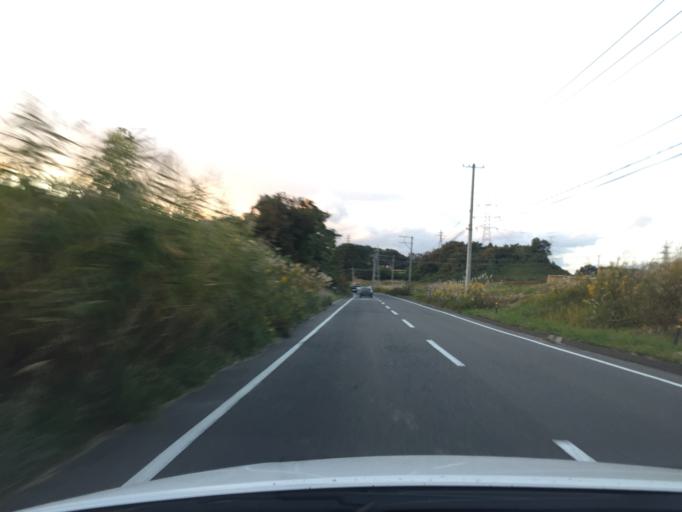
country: JP
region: Fukushima
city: Miharu
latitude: 37.3865
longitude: 140.4475
